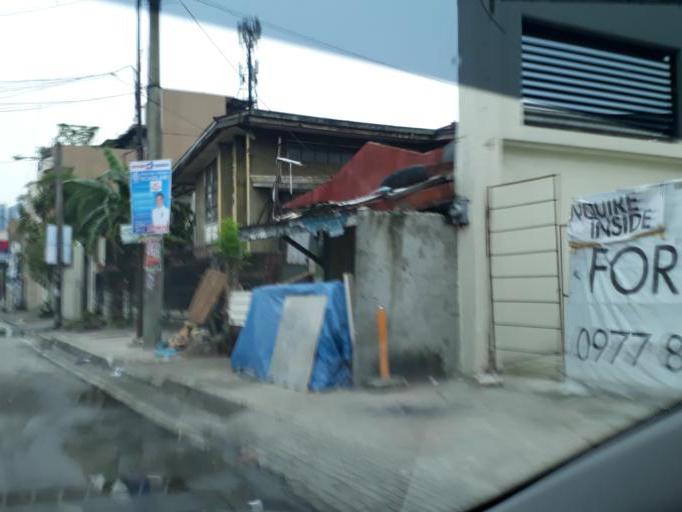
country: PH
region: Calabarzon
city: Del Monte
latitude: 14.6283
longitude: 120.9967
